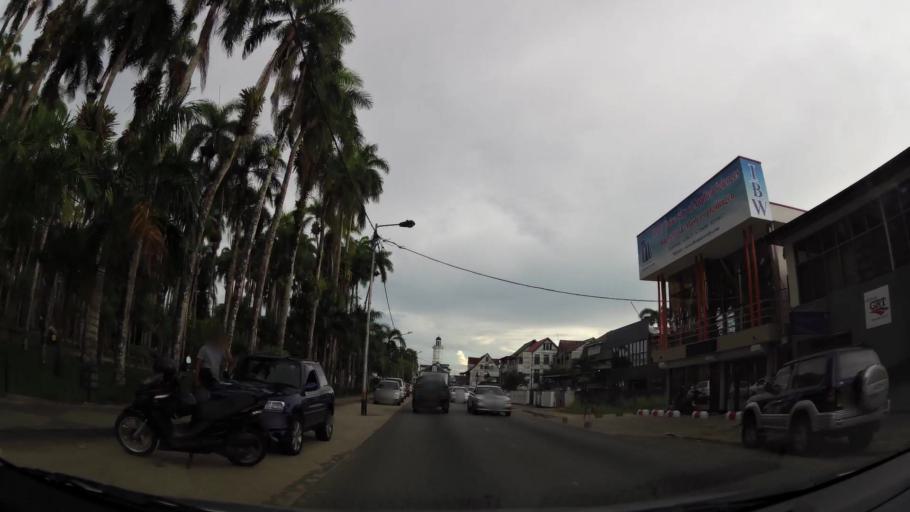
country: SR
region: Paramaribo
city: Paramaribo
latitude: 5.8289
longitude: -55.1509
